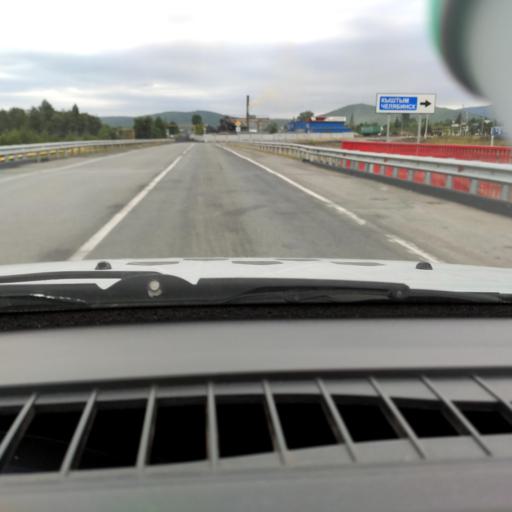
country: RU
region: Chelyabinsk
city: Karabash
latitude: 55.4464
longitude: 60.2251
